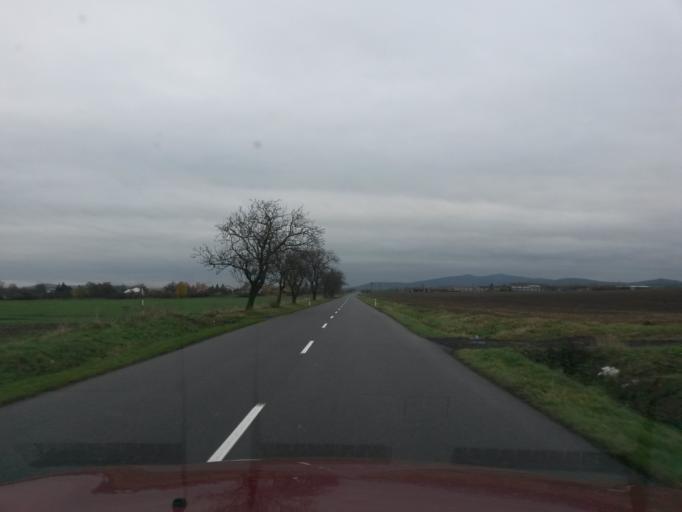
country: SK
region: Kosicky
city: Trebisov
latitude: 48.5722
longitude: 21.6456
